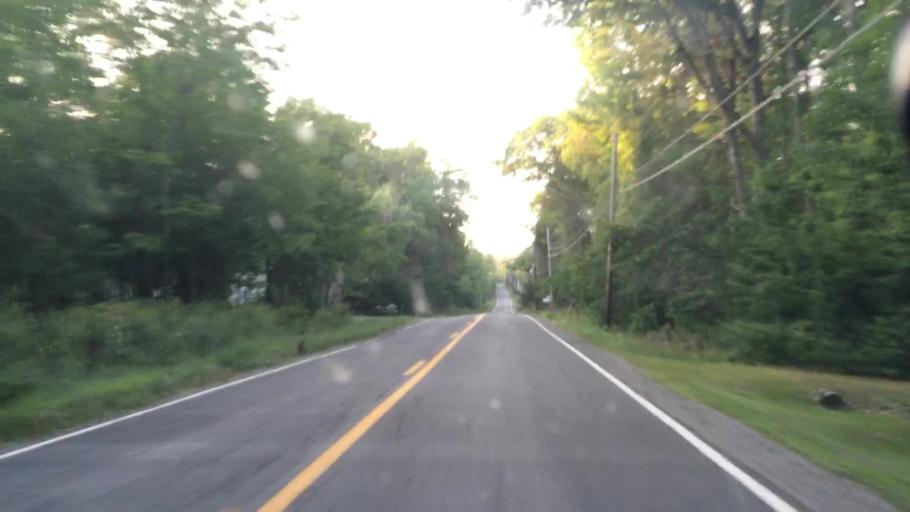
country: US
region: Maine
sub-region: Penobscot County
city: Hermon
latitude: 44.7013
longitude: -68.9460
